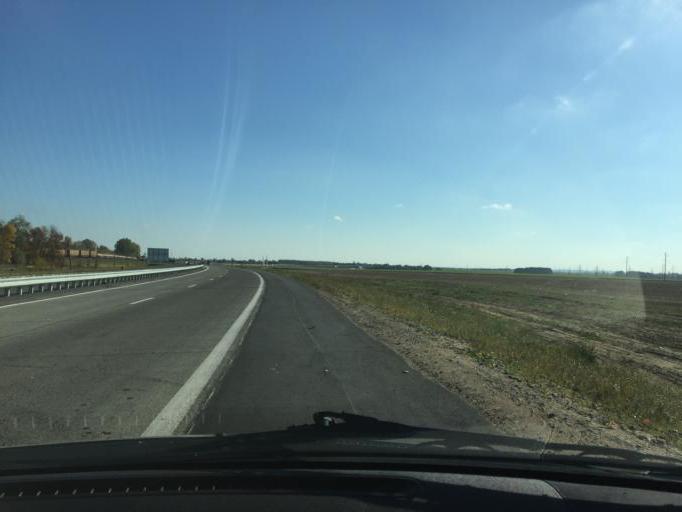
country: BY
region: Minsk
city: Slutsk
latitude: 53.0056
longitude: 27.4897
